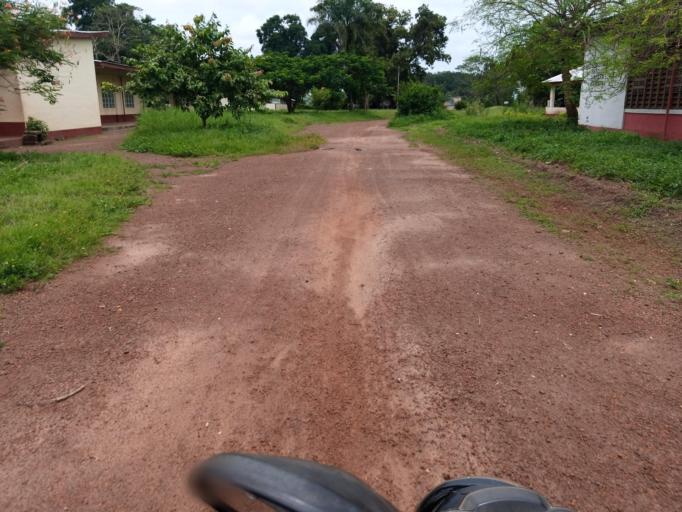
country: SL
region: Southern Province
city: Largo
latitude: 8.1982
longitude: -12.0635
